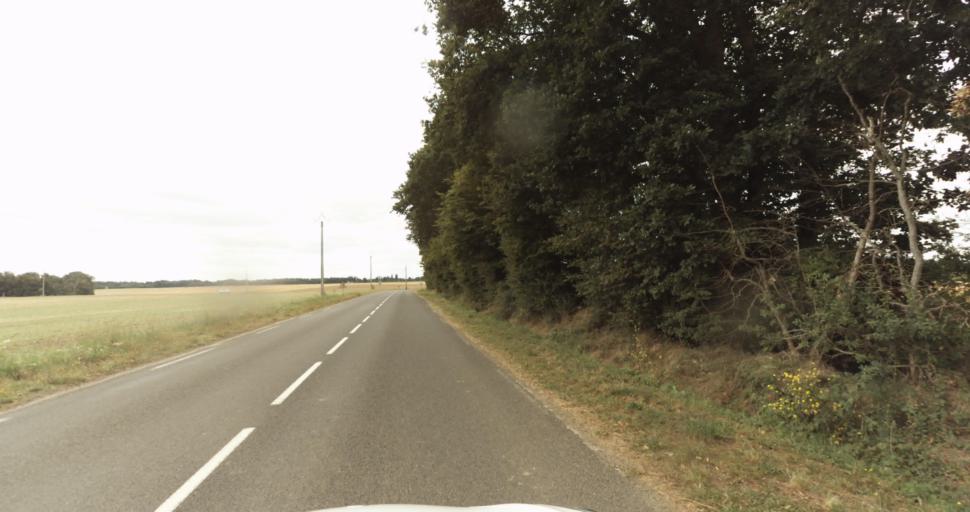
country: FR
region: Haute-Normandie
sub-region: Departement de l'Eure
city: La Madeleine-de-Nonancourt
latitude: 48.8402
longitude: 1.2404
